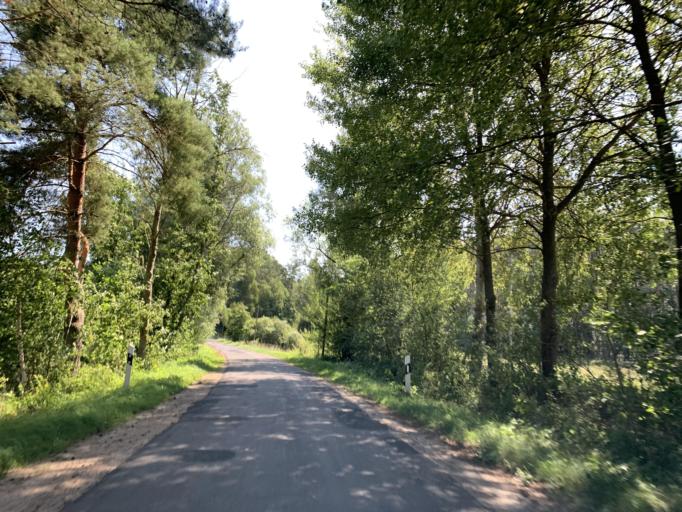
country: DE
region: Mecklenburg-Vorpommern
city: Carpin
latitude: 53.3213
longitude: 13.2442
